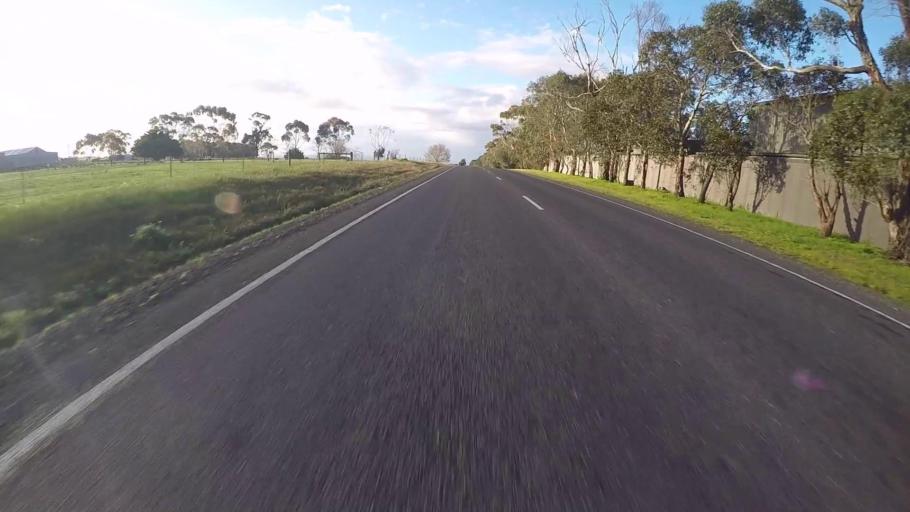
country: AU
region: Victoria
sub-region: Greater Geelong
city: Wandana Heights
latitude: -38.1673
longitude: 144.1610
